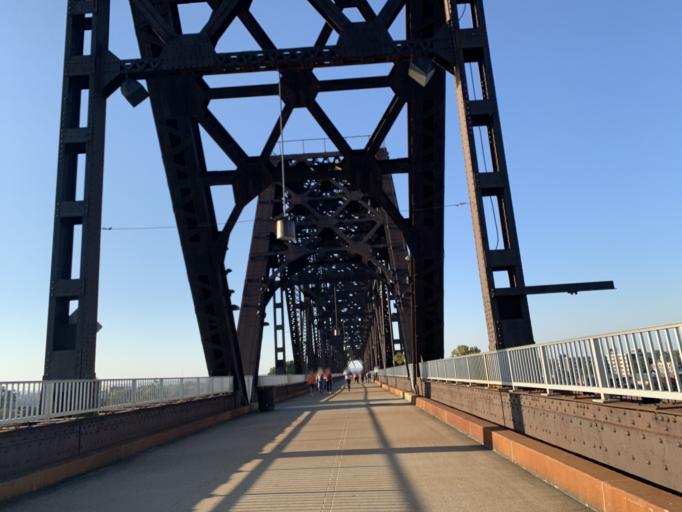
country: US
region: Indiana
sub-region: Clark County
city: Jeffersonville
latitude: 38.2661
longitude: -85.7396
